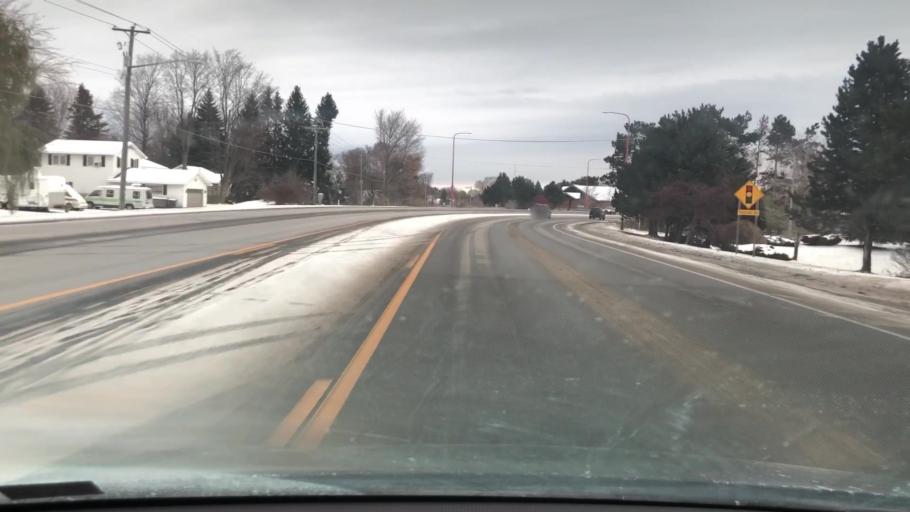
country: US
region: Michigan
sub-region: Grand Traverse County
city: Traverse City
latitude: 44.7291
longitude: -85.6359
